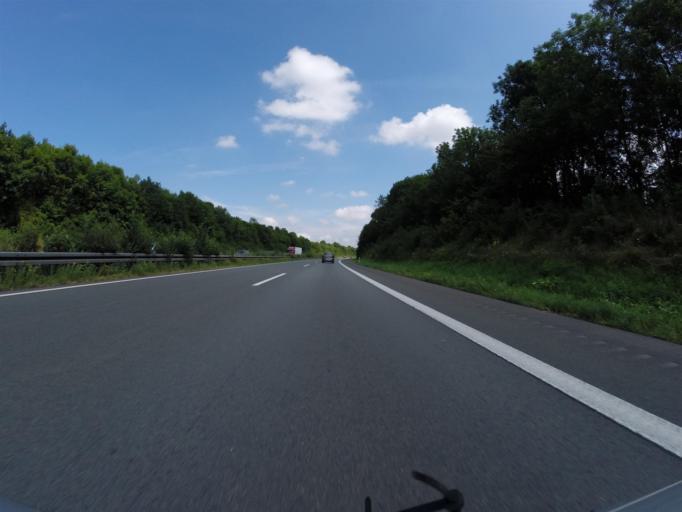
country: DE
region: North Rhine-Westphalia
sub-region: Regierungsbezirk Detmold
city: Paderborn
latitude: 51.6629
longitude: 8.7075
